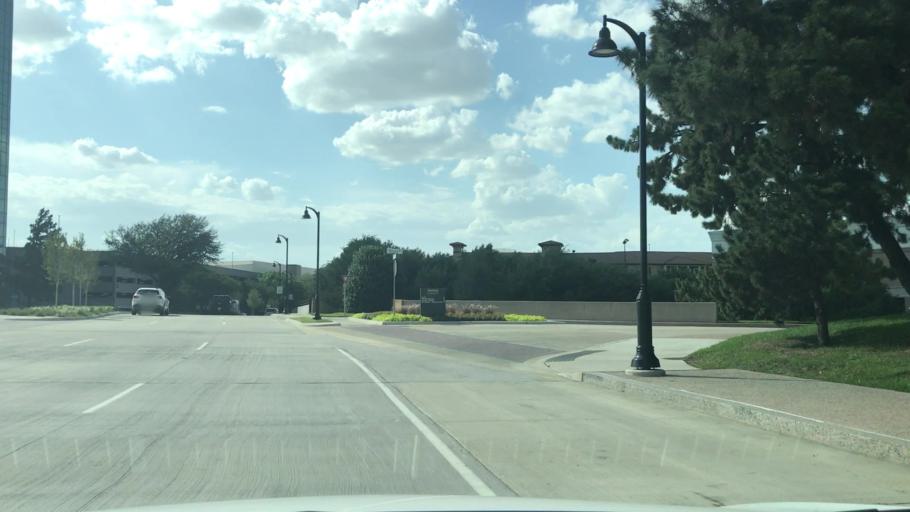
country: US
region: Texas
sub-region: Dallas County
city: Irving
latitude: 32.8706
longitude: -96.9415
